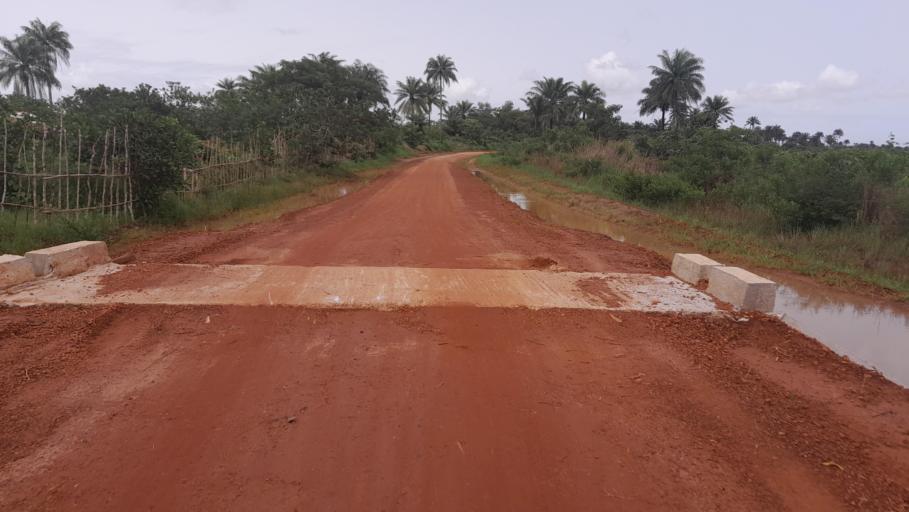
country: GN
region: Boke
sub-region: Boffa
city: Boffa
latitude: 10.0596
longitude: -13.8683
